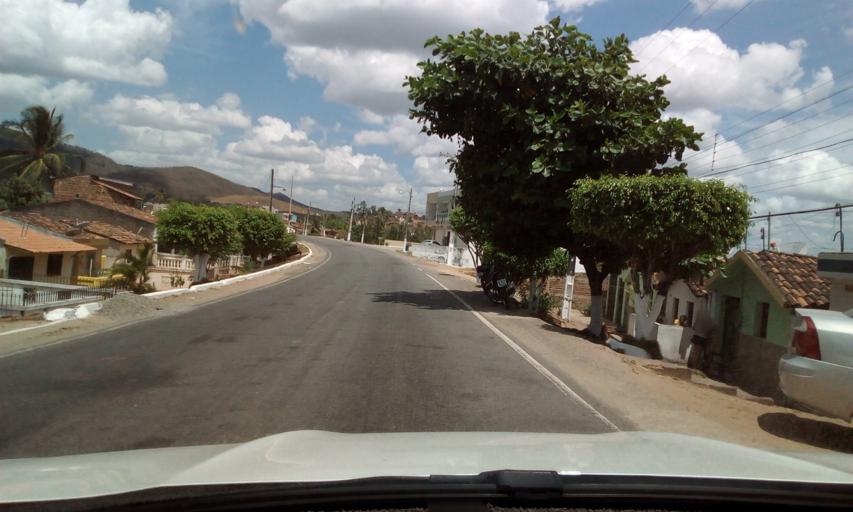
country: BR
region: Paraiba
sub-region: Alagoinha
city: Alagoinha
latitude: -6.9016
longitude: -35.5258
